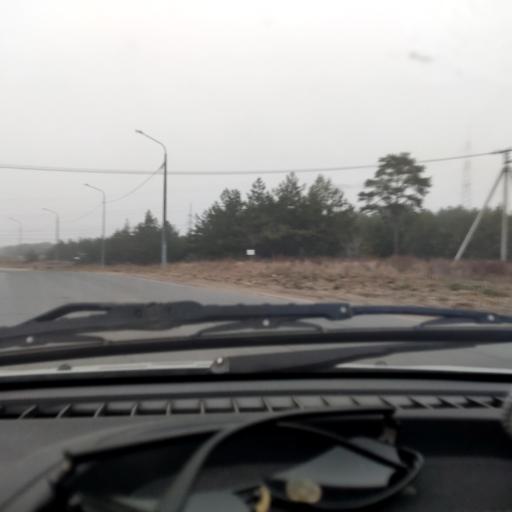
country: RU
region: Samara
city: Zhigulevsk
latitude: 53.4867
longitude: 49.5369
